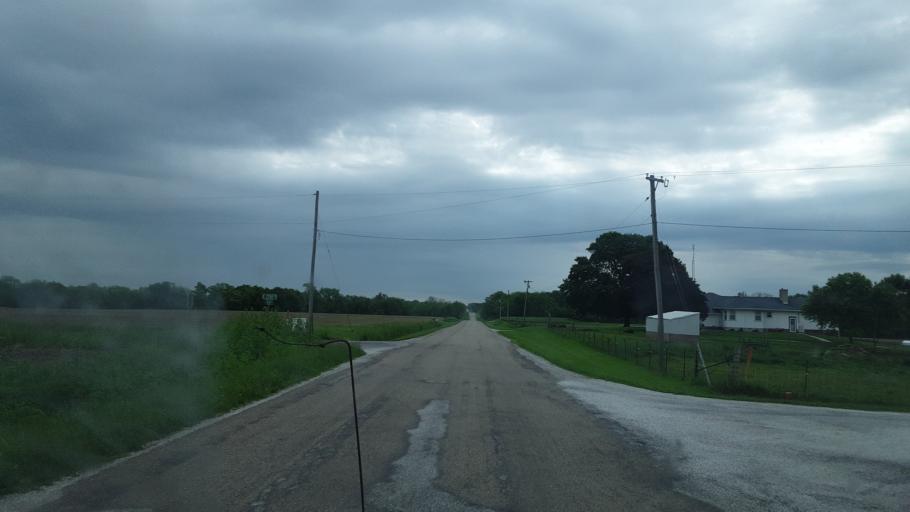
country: US
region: Illinois
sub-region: Fulton County
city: Astoria
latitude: 40.3644
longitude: -90.4586
